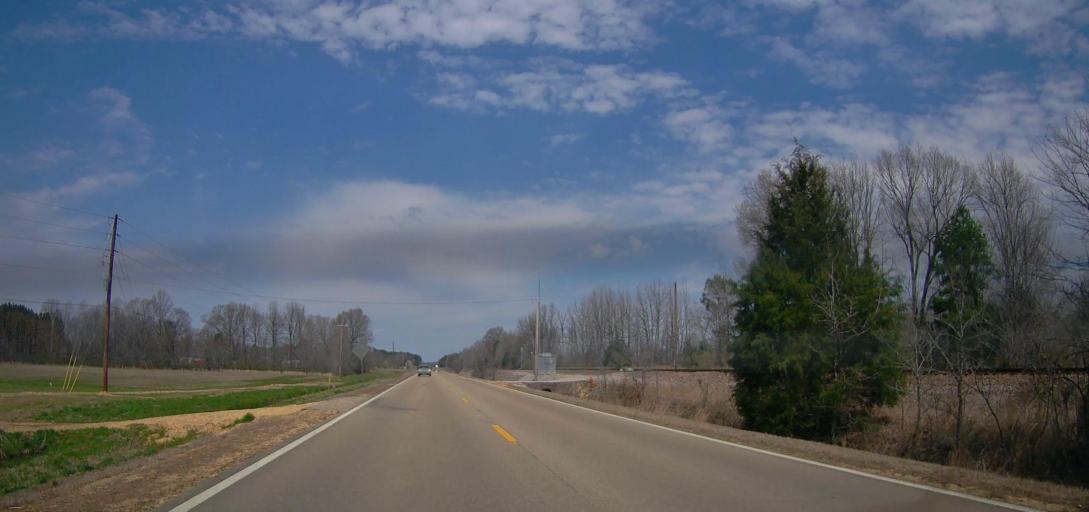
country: US
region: Mississippi
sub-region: Union County
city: New Albany
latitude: 34.5743
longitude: -89.1290
